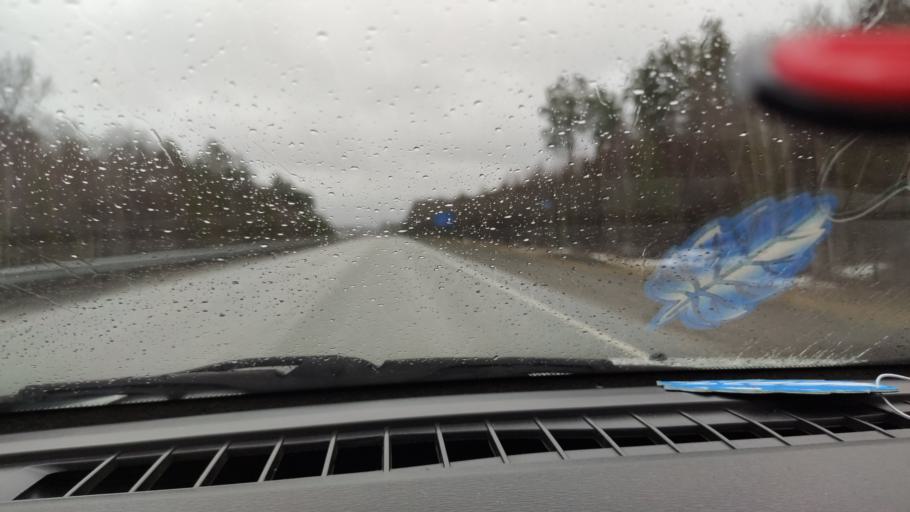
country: RU
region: Sverdlovsk
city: Ufimskiy
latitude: 56.7753
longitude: 57.9970
